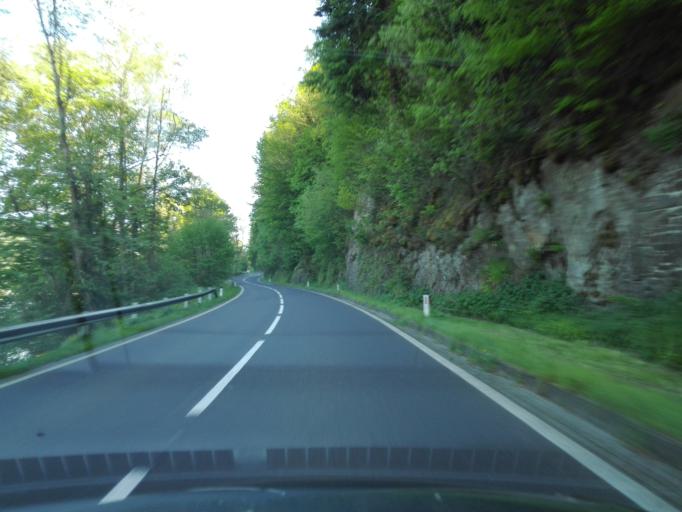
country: AT
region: Upper Austria
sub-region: Politischer Bezirk Rohrbach
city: Pfarrkirchen im Muehlkreis
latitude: 48.4674
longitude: 13.7775
